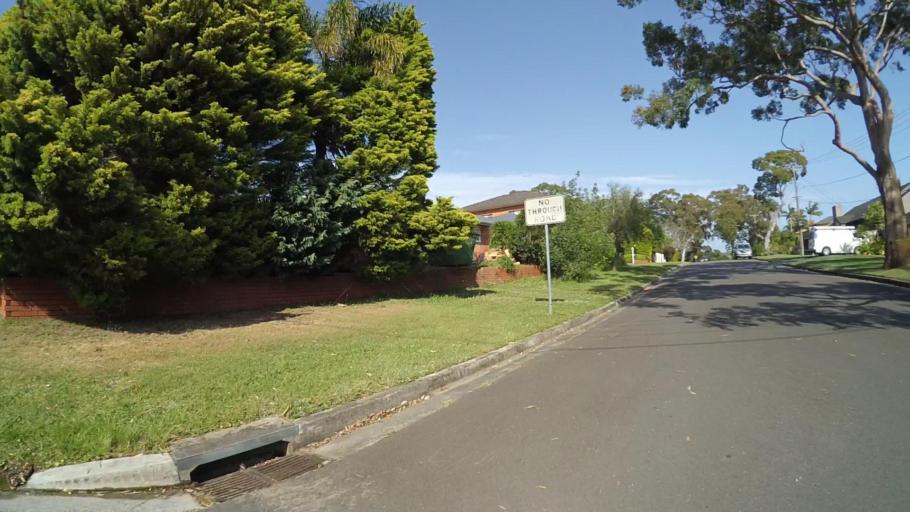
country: AU
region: New South Wales
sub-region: Sutherland Shire
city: Dolans Bay
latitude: -34.0673
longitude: 151.1378
